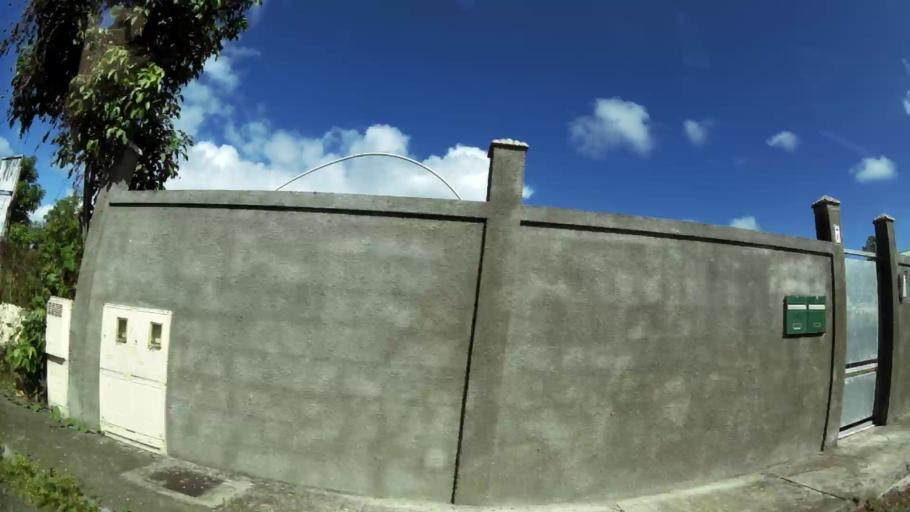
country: GP
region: Guadeloupe
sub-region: Guadeloupe
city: Port-Louis
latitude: 16.4139
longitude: -61.5269
